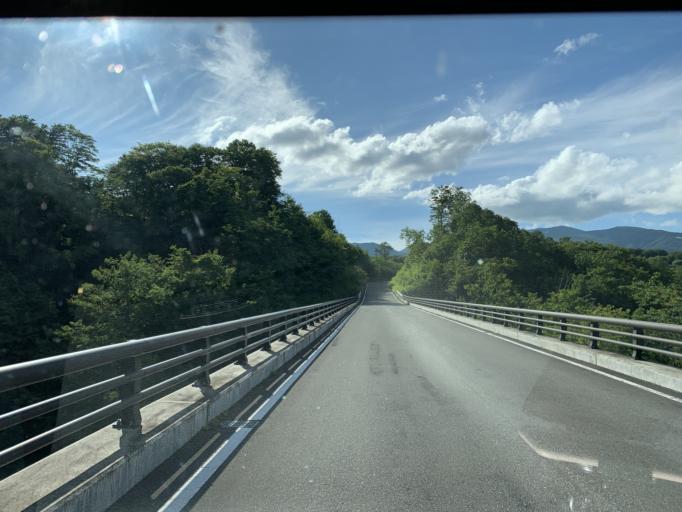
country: JP
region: Iwate
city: Ichinoseki
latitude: 38.9074
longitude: 140.8395
